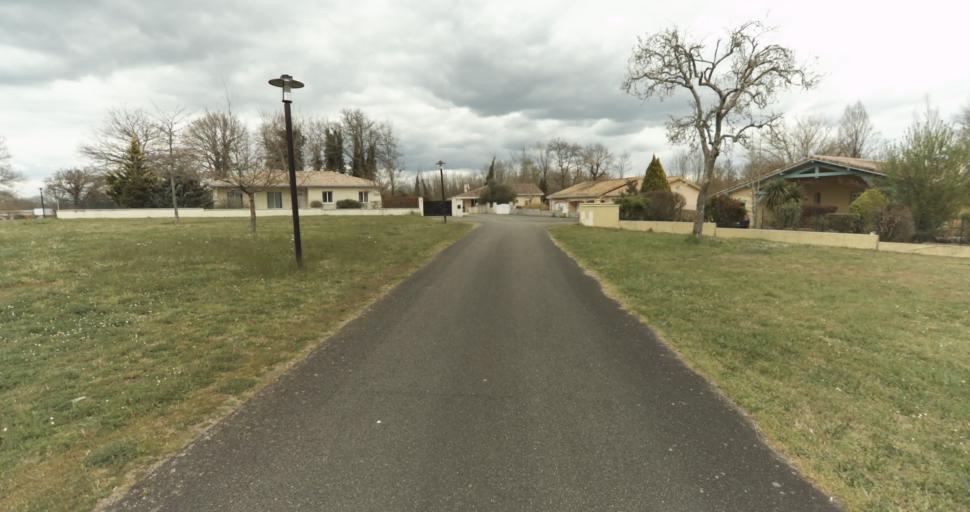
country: FR
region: Aquitaine
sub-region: Departement des Landes
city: Roquefort
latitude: 44.0344
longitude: -0.3147
